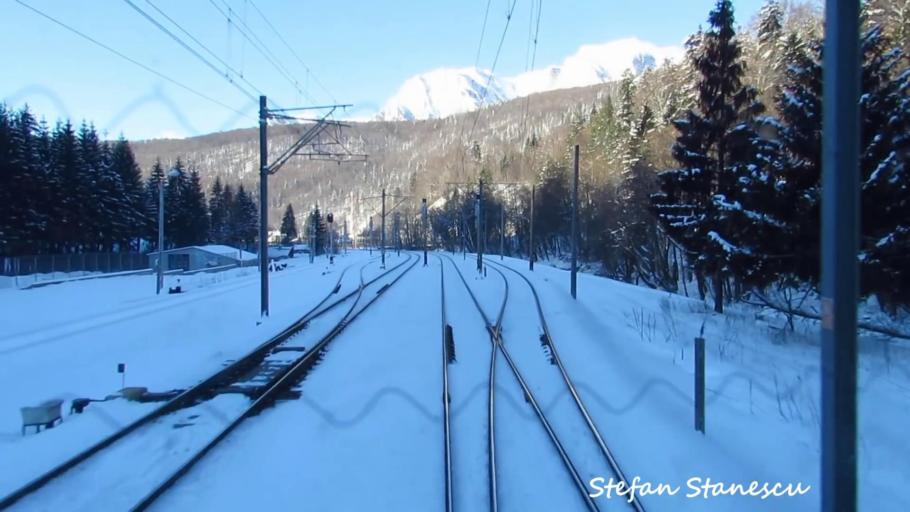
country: RO
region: Prahova
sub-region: Oras Azuga
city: Azuga
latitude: 45.4500
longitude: 25.5586
